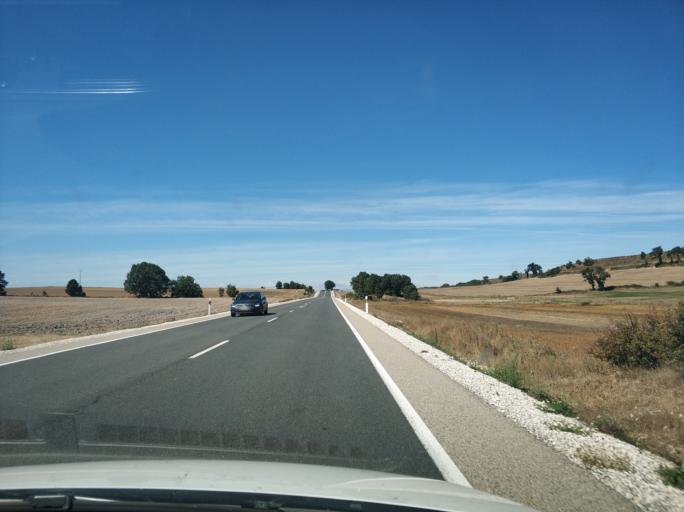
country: ES
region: Castille and Leon
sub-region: Provincia de Burgos
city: Basconcillos del Tozo
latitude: 42.6691
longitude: -3.9265
